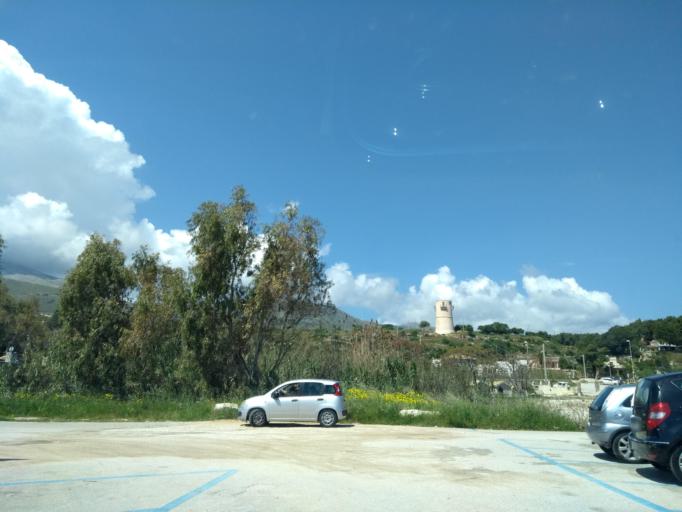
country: IT
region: Sicily
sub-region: Trapani
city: Castellammare del Golfo
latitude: 38.0562
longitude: 12.8400
